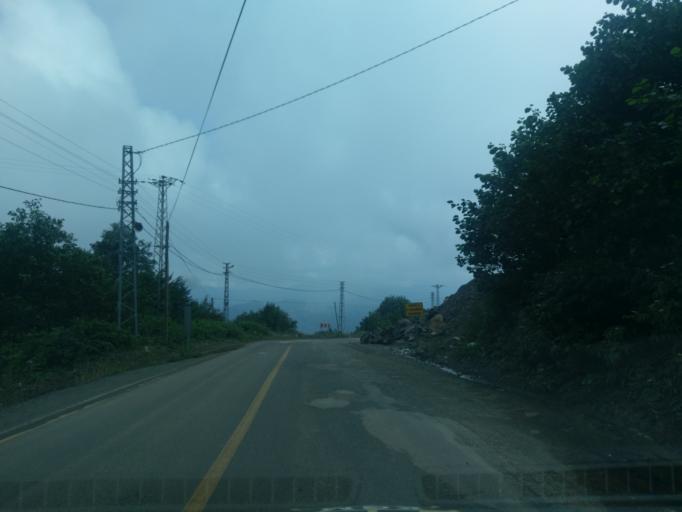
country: TR
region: Ordu
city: Gurgentepe
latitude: 40.8521
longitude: 37.6599
